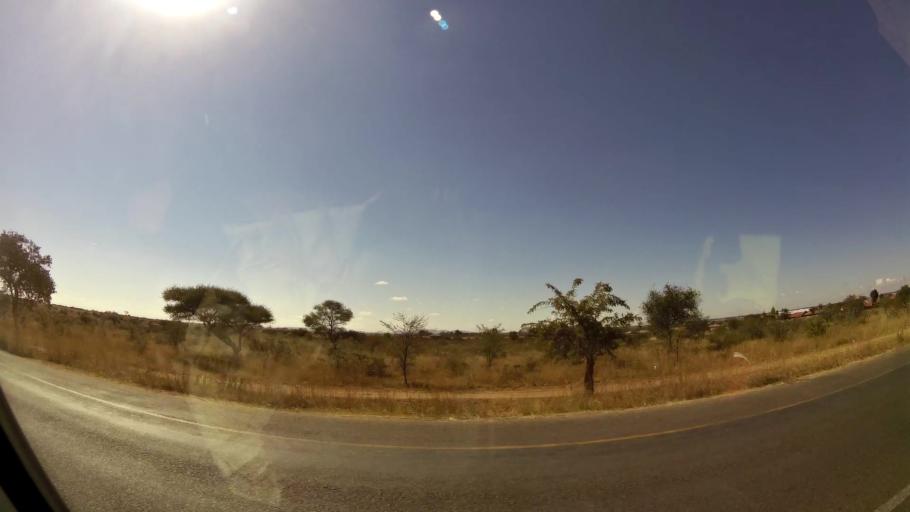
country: ZA
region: Limpopo
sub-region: Capricorn District Municipality
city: Polokwane
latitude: -23.8666
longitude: 29.4216
